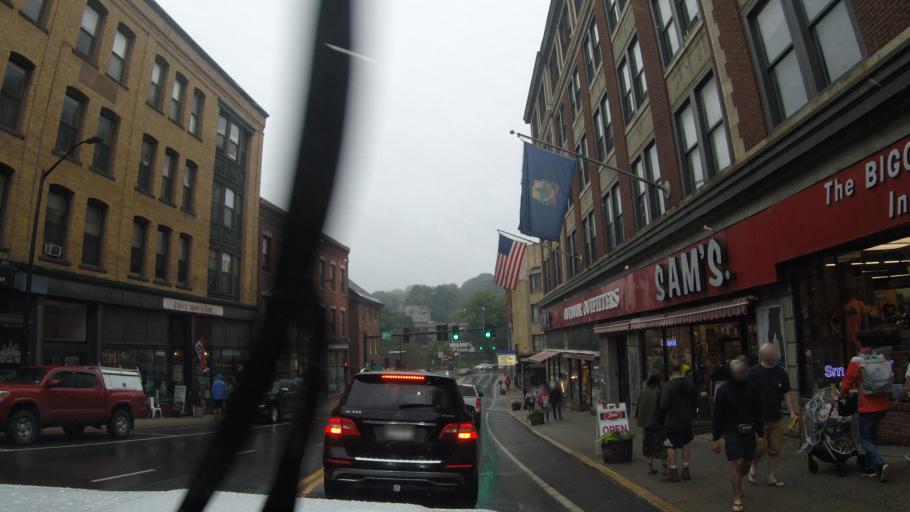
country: US
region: Vermont
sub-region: Windham County
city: Brattleboro
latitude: 42.8521
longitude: -72.5578
